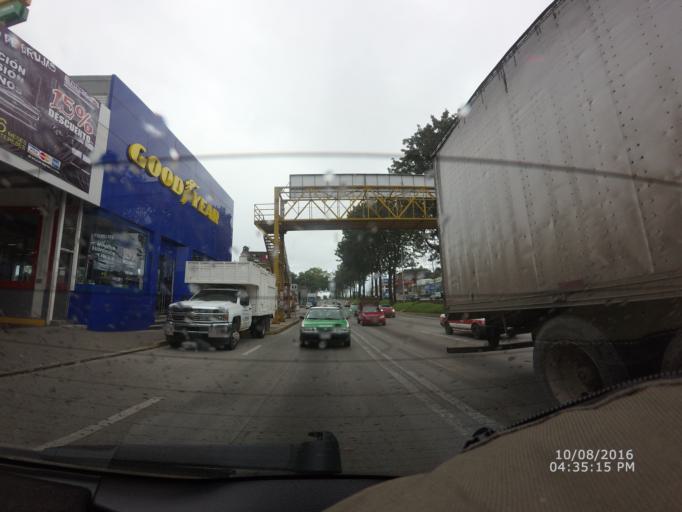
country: MX
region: Veracruz
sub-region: Xalapa
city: Xalapa de Enriquez
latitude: 19.5599
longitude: -96.9218
